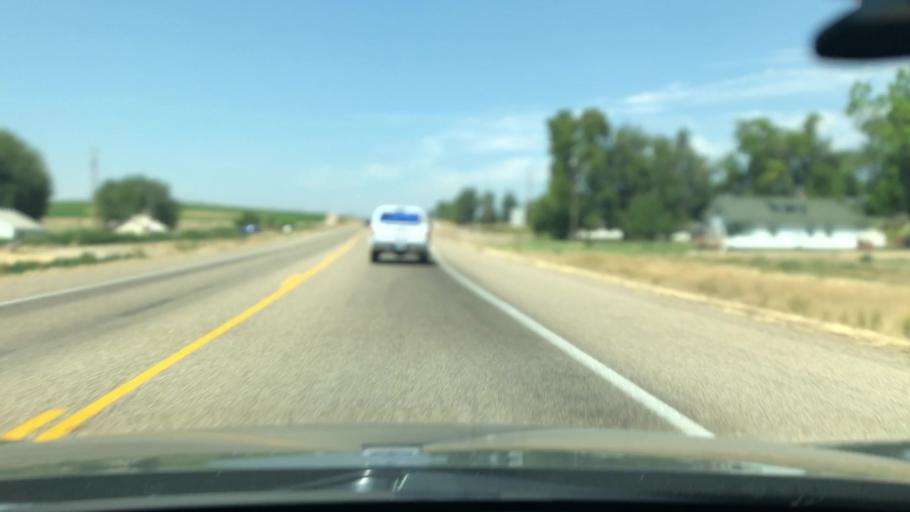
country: US
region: Idaho
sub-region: Canyon County
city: Parma
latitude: 43.8157
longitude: -116.9543
